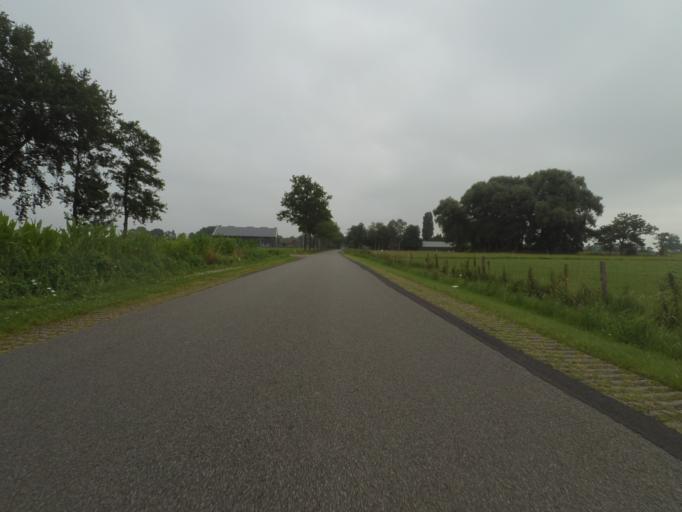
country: NL
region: Gelderland
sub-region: Gemeente Barneveld
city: Kootwijkerbroek
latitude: 52.1343
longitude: 5.6302
